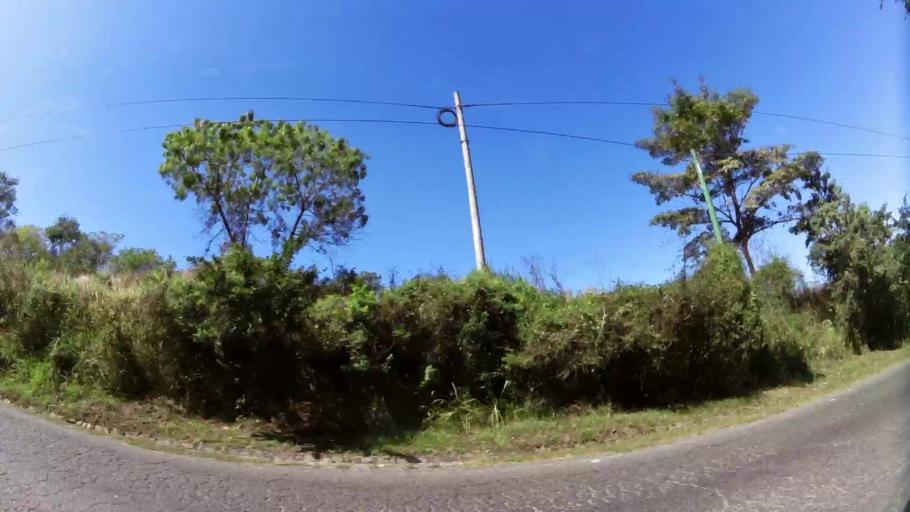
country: SV
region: Ahuachapan
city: Ahuachapan
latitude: 13.9452
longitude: -89.8231
